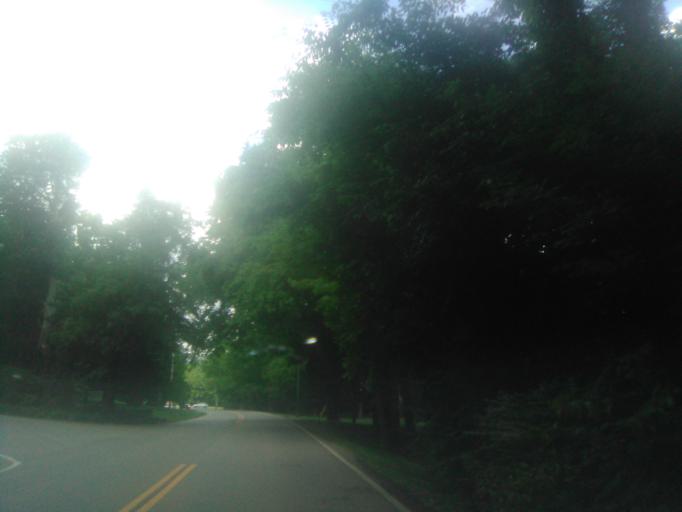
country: US
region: Tennessee
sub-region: Davidson County
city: Belle Meade
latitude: 36.1022
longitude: -86.8452
